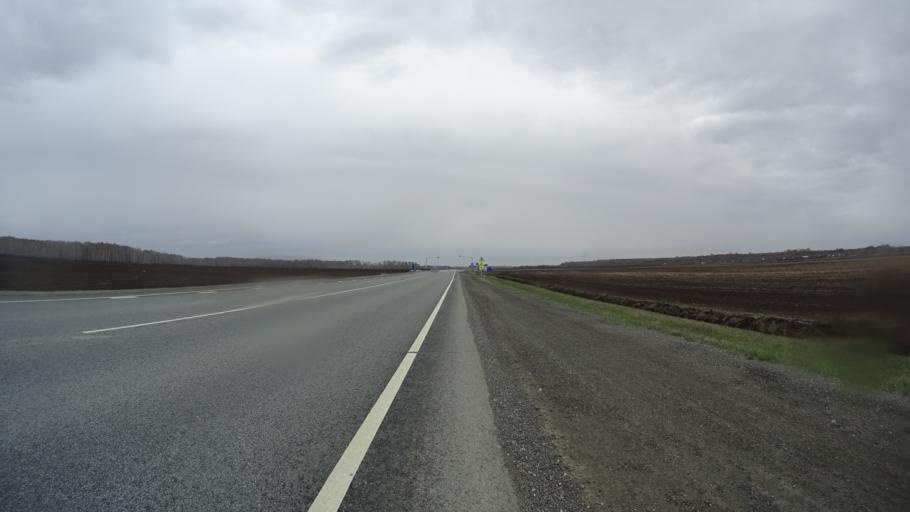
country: RU
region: Chelyabinsk
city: Krasnogorskiy
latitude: 54.5836
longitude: 61.2910
